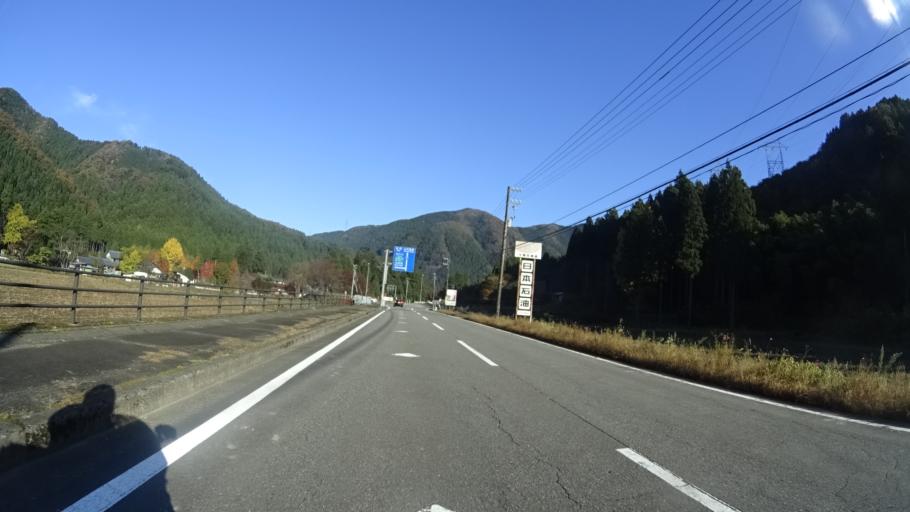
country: JP
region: Fukui
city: Maruoka
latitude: 36.1648
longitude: 136.3322
